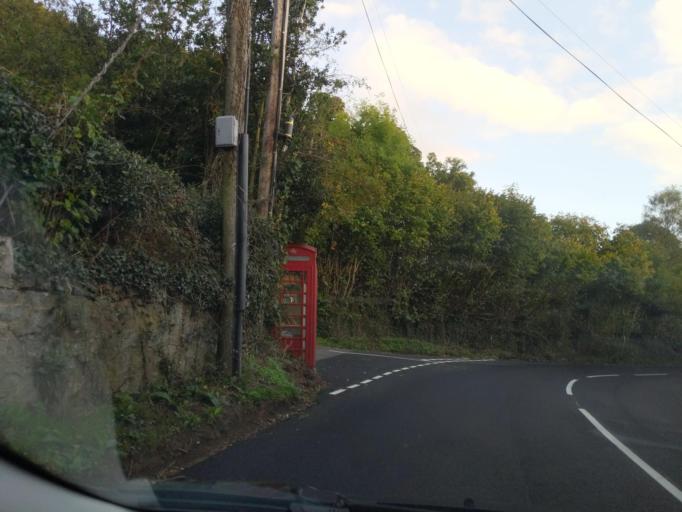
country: GB
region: England
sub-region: Devon
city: Bovey Tracey
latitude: 50.6127
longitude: -3.6945
